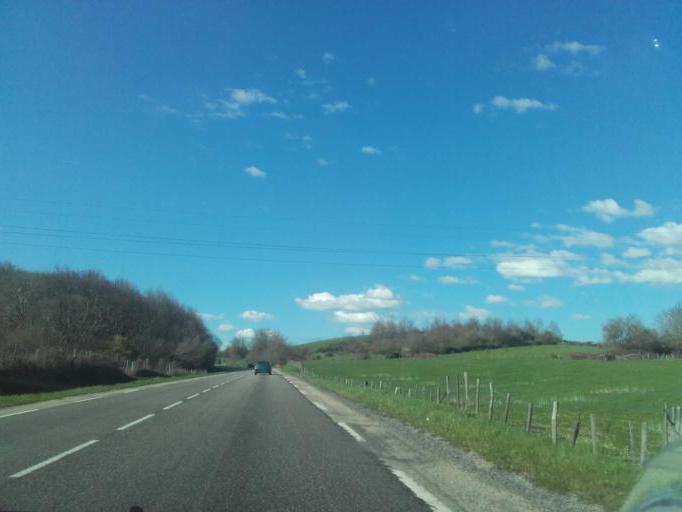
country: FR
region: Rhone-Alpes
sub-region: Departement de l'Isere
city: Champier
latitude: 45.4774
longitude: 5.2926
